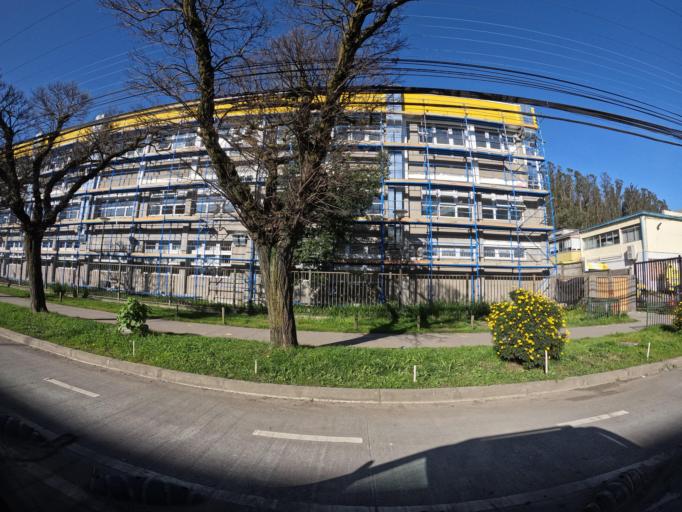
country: CL
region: Biobio
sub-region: Provincia de Concepcion
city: Concepcion
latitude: -36.8244
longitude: -73.0367
